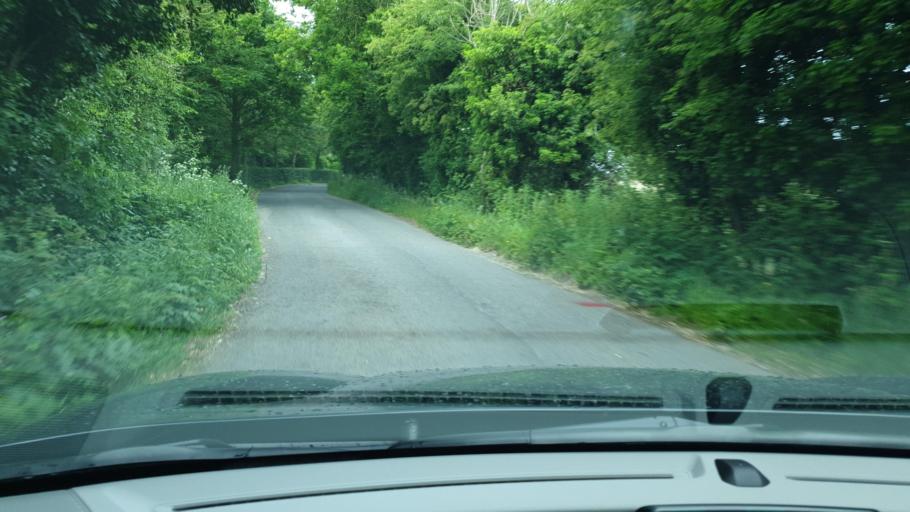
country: IE
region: Leinster
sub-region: An Mhi
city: Ashbourne
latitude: 53.5245
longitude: -6.3887
